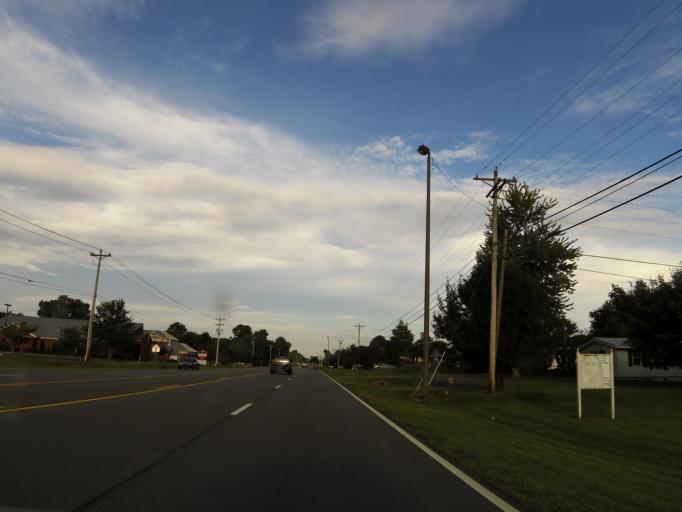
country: US
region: Alabama
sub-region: Limestone County
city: Athens
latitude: 34.7907
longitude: -86.9970
